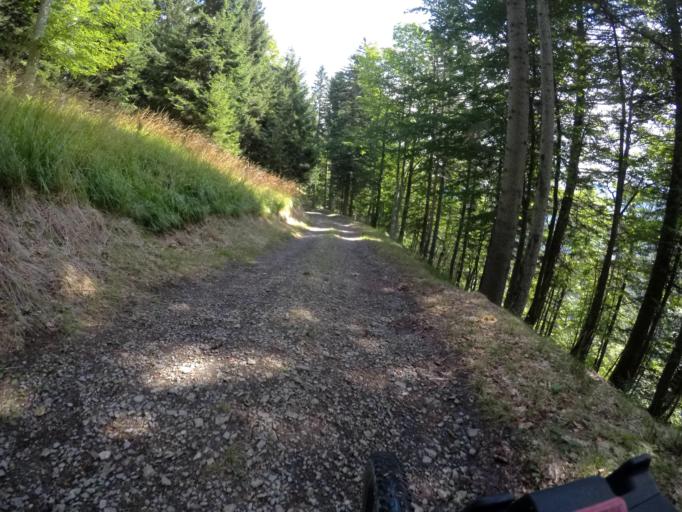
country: IT
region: Friuli Venezia Giulia
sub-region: Provincia di Udine
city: Paularo
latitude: 46.5022
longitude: 13.1722
